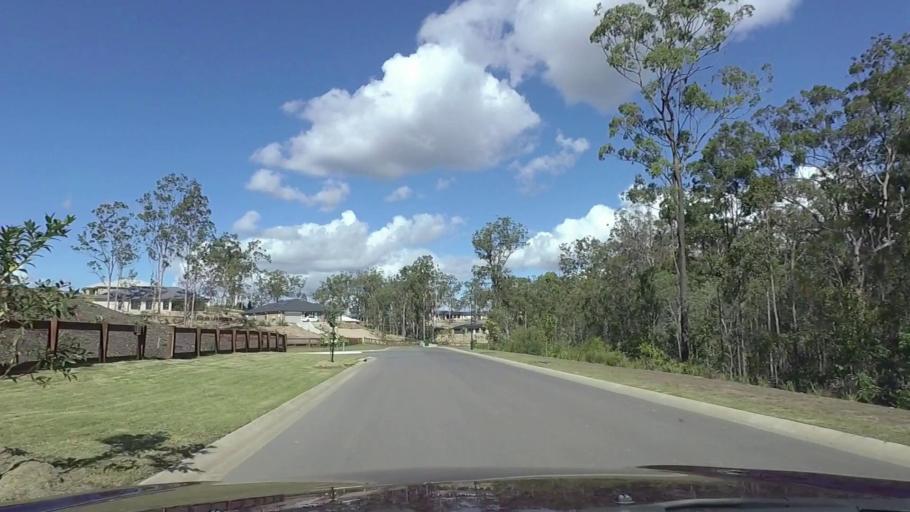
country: AU
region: Queensland
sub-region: Ipswich
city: Springfield Lakes
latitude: -27.7490
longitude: 152.9206
